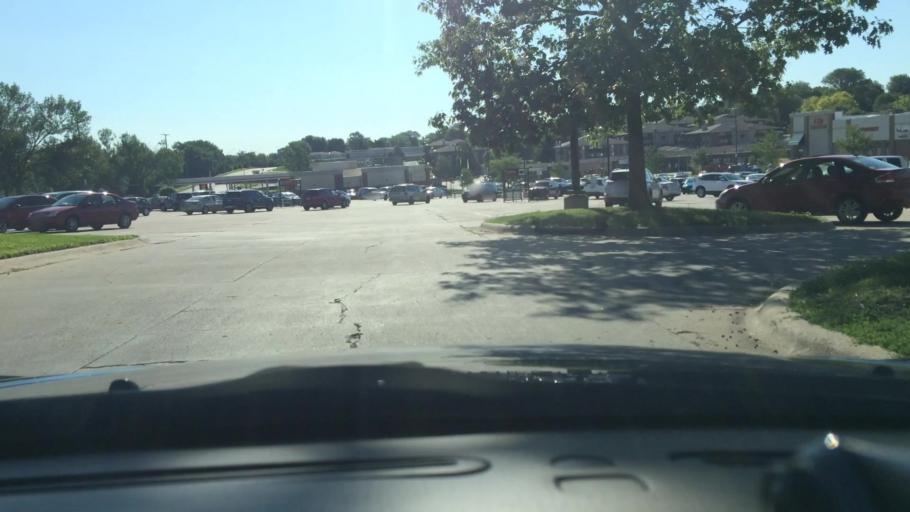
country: US
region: Nebraska
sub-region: Douglas County
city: Ralston
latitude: 41.2047
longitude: -96.0646
